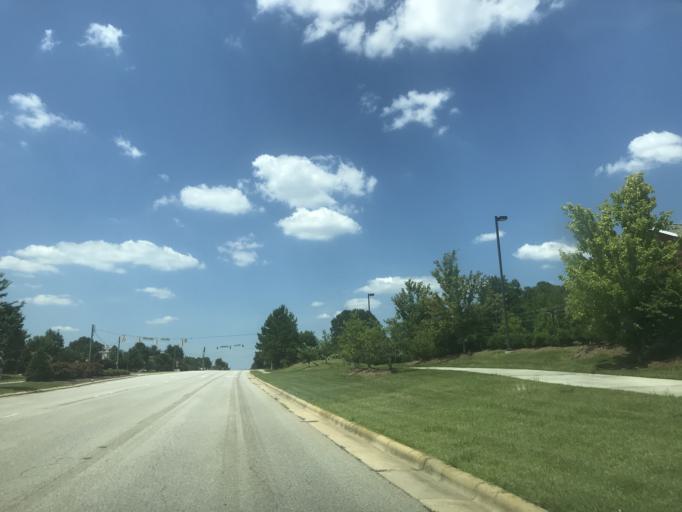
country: US
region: North Carolina
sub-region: Wake County
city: Cary
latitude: 35.7489
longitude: -78.7408
